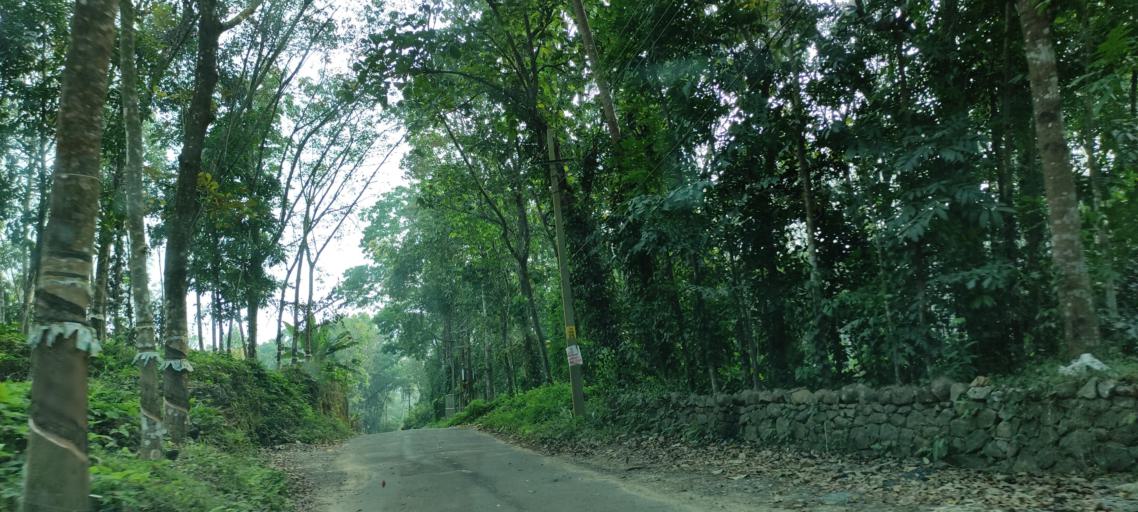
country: IN
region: Kerala
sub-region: Ernakulam
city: Piravam
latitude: 9.8059
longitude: 76.5357
